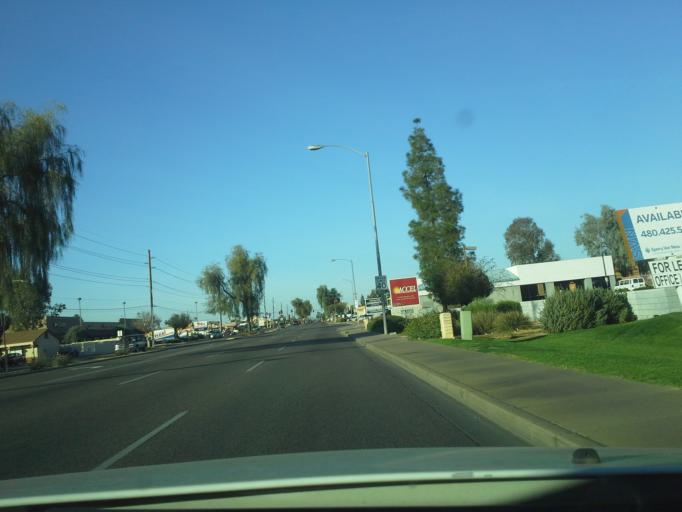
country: US
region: Arizona
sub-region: Maricopa County
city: Glendale
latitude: 33.5791
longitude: -112.1340
